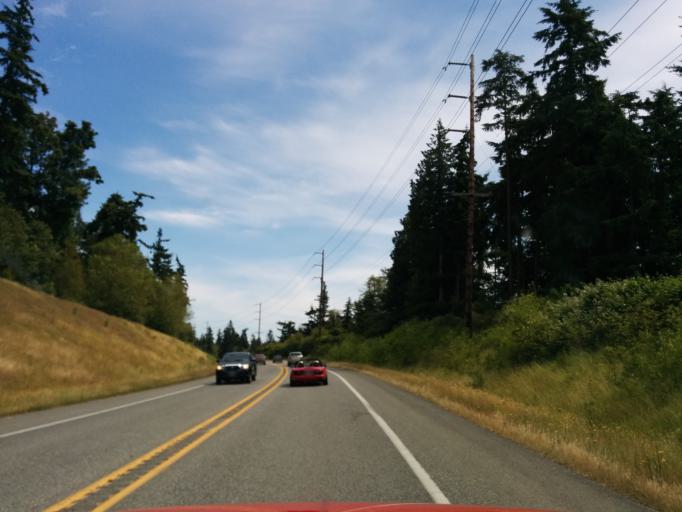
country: US
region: Washington
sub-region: Island County
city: Freeland
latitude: 48.0227
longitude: -122.5580
